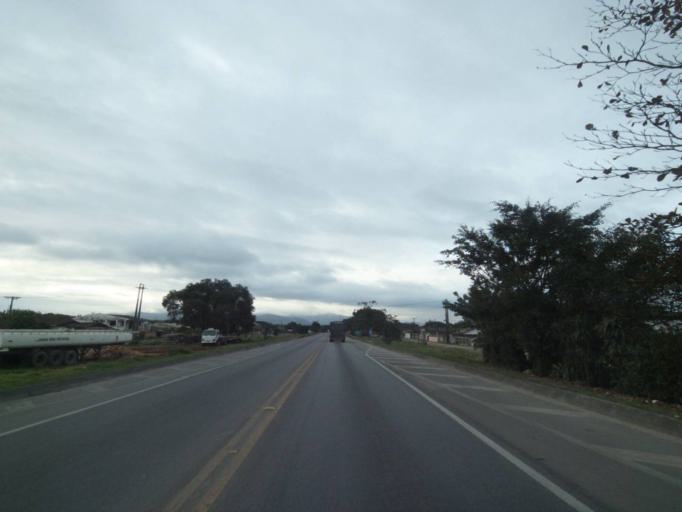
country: BR
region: Parana
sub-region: Paranagua
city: Paranagua
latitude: -25.5261
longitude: -48.5475
